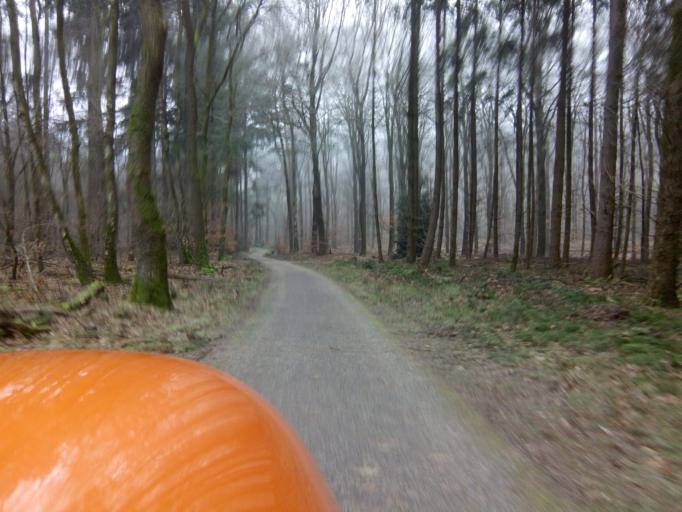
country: NL
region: Gelderland
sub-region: Gemeente Barneveld
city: Garderen
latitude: 52.2562
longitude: 5.6895
